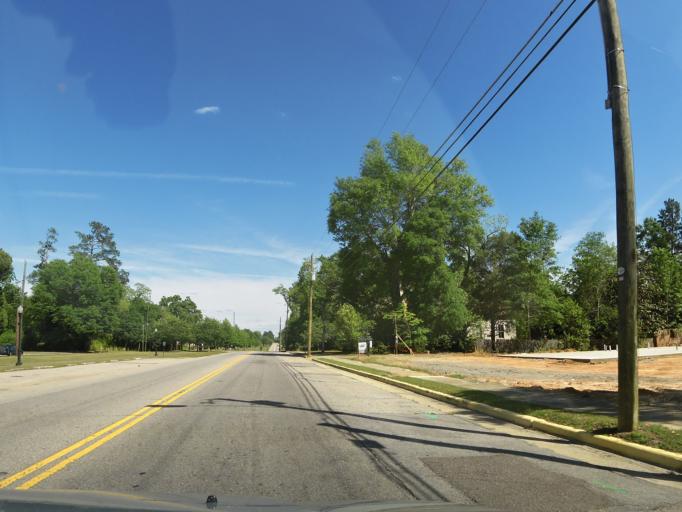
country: US
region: South Carolina
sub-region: Barnwell County
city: Williston
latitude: 33.3999
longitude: -81.4187
